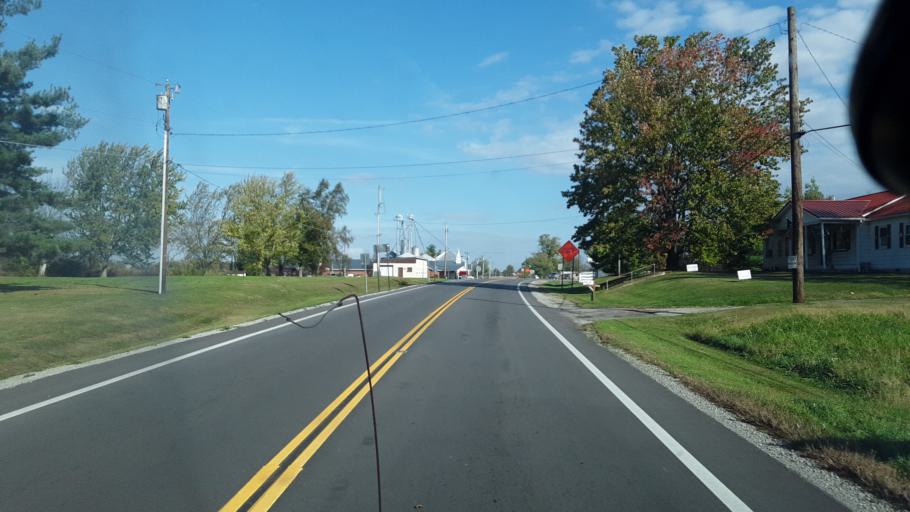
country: US
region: Ohio
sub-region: Highland County
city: Leesburg
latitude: 39.2887
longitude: -83.5912
